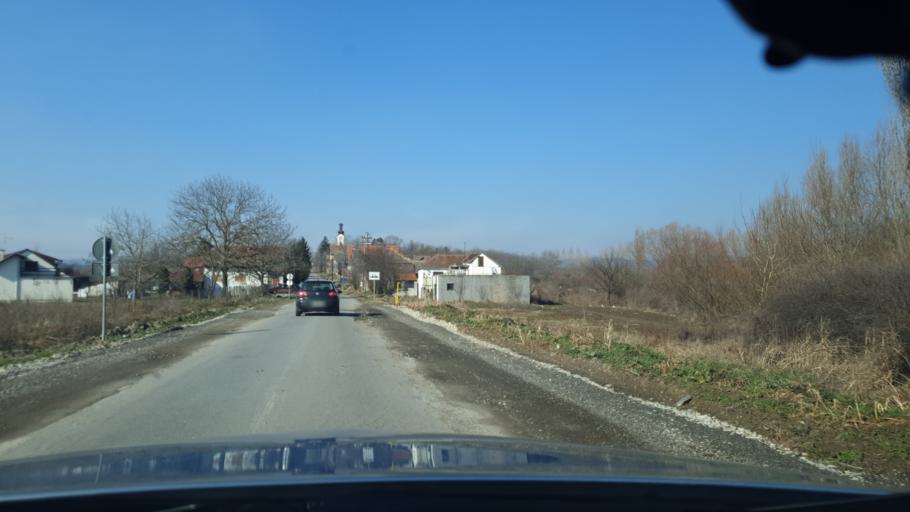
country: RS
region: Autonomna Pokrajina Vojvodina
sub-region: Sremski Okrug
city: Irig
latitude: 45.0856
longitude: 19.8377
